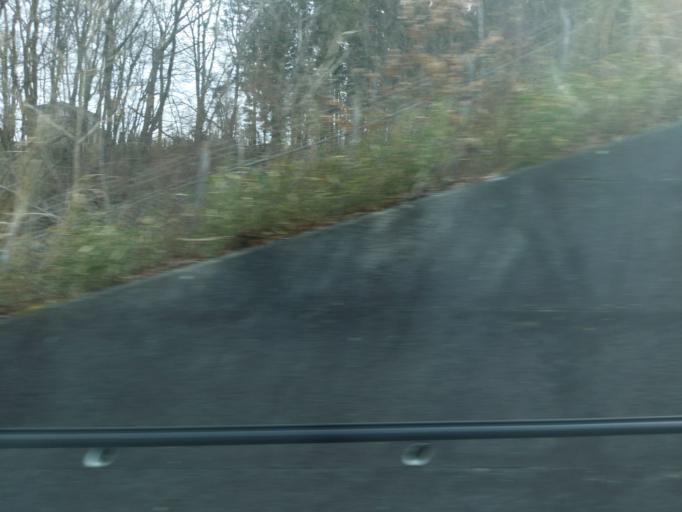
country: JP
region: Miyagi
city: Kogota
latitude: 38.7332
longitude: 141.0629
